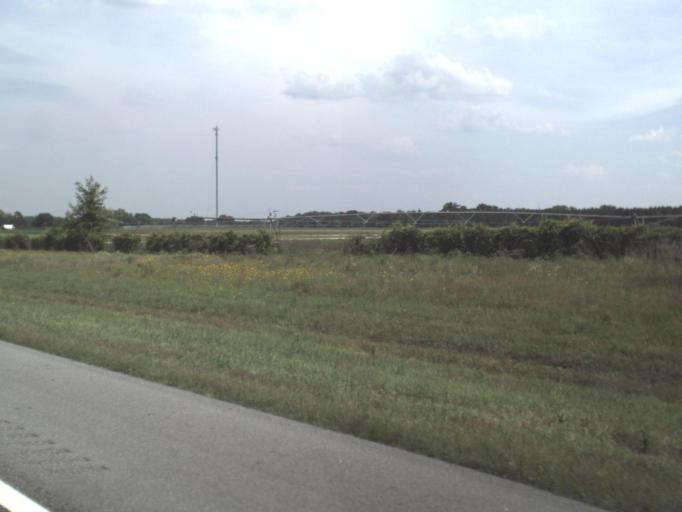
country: US
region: Florida
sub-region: Suwannee County
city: Live Oak
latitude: 30.3515
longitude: -83.0255
